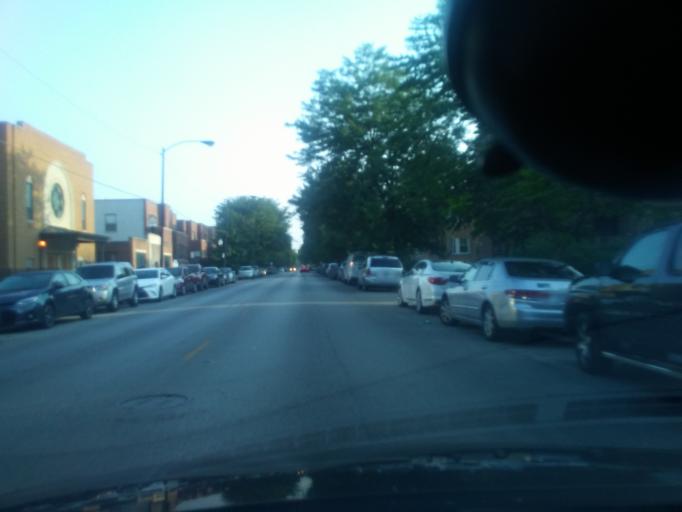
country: US
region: Illinois
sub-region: Cook County
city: Lincolnwood
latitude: 41.9995
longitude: -87.6998
